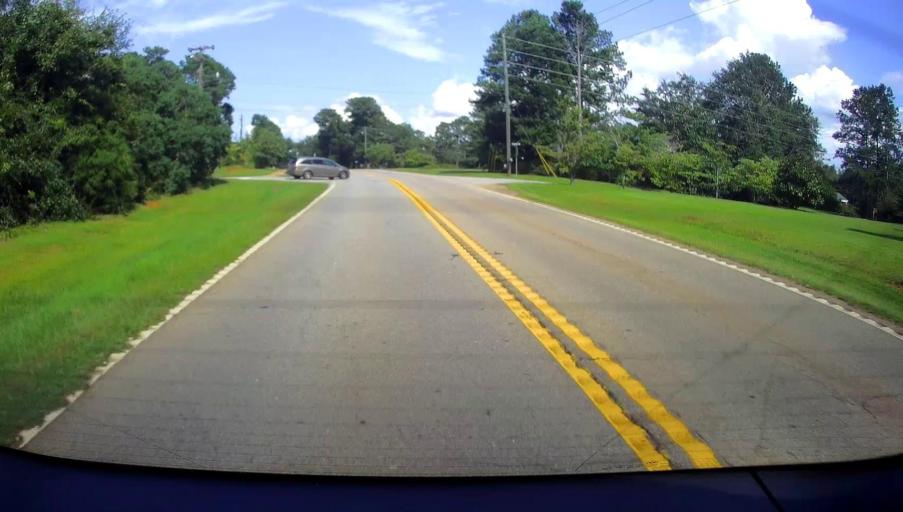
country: US
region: Georgia
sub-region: Upson County
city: Thomaston
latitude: 32.8762
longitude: -84.3409
